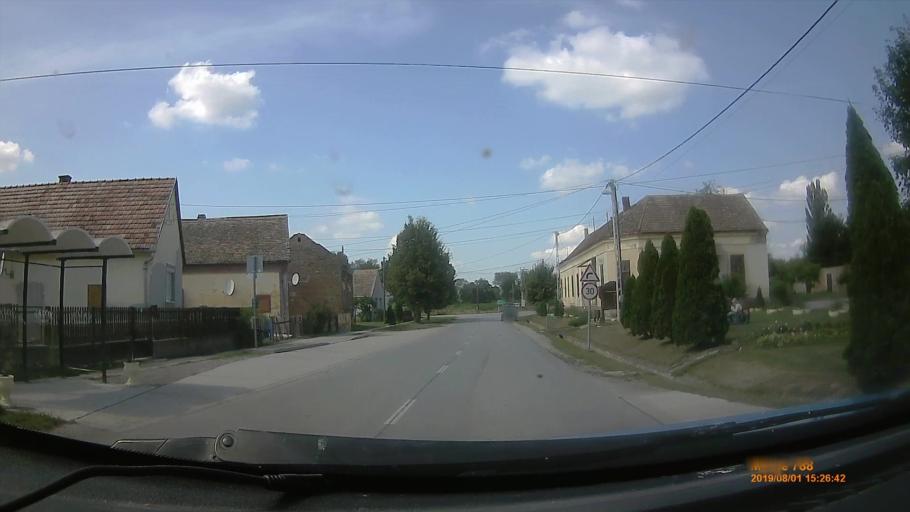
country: HU
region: Baranya
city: Sellye
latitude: 45.9033
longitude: 17.8580
